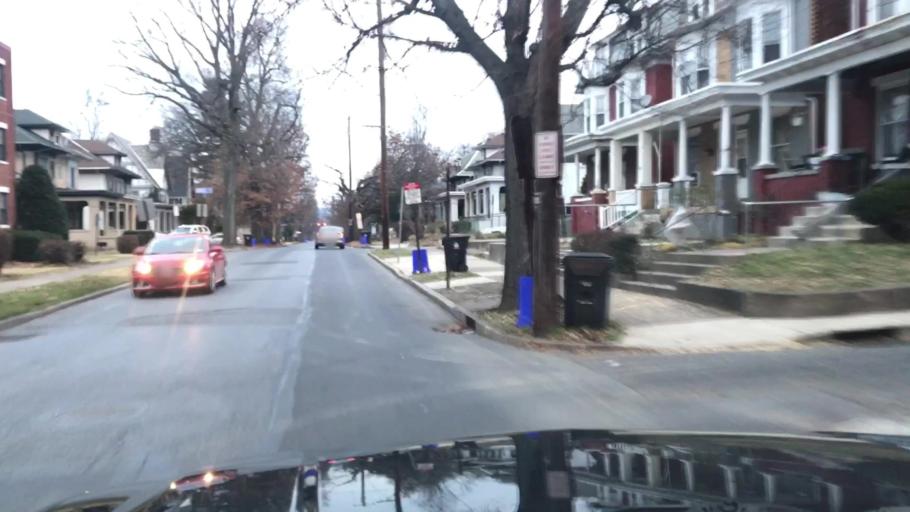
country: US
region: Pennsylvania
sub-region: Dauphin County
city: Harrisburg
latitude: 40.2730
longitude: -76.8675
